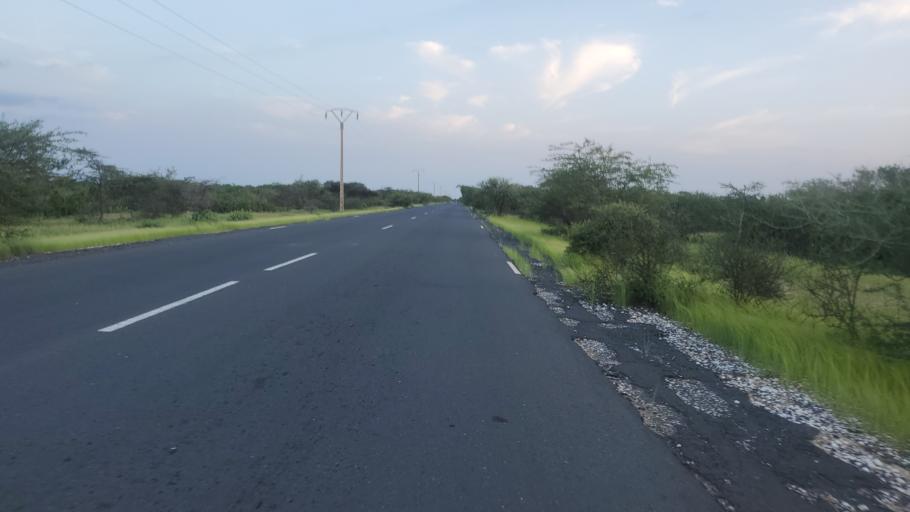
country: SN
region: Saint-Louis
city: Saint-Louis
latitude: 16.1164
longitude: -16.4137
